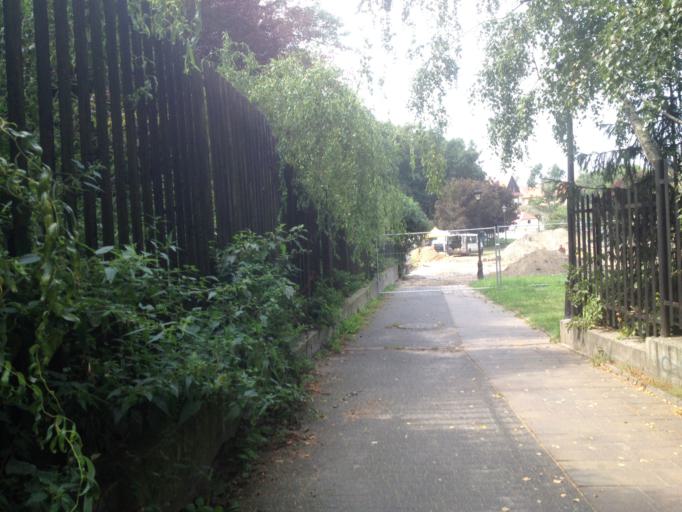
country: PL
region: Greater Poland Voivodeship
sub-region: Powiat gnieznienski
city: Gniezno
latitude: 52.5373
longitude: 17.5972
